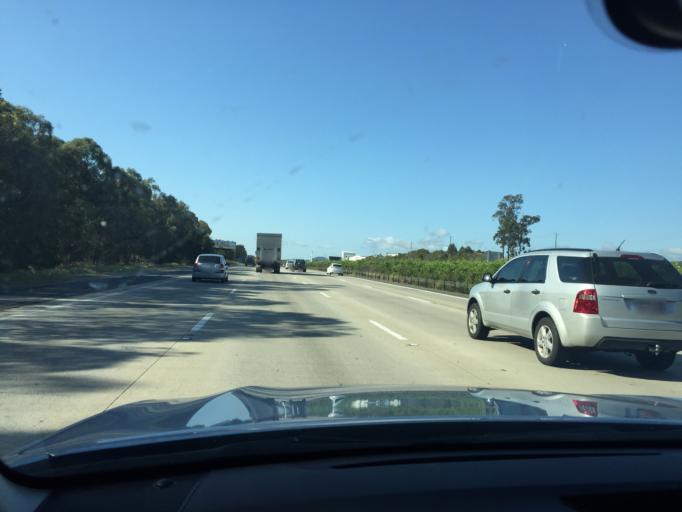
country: AU
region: Queensland
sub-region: Gold Coast
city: Yatala
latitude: -27.7455
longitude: 153.2337
